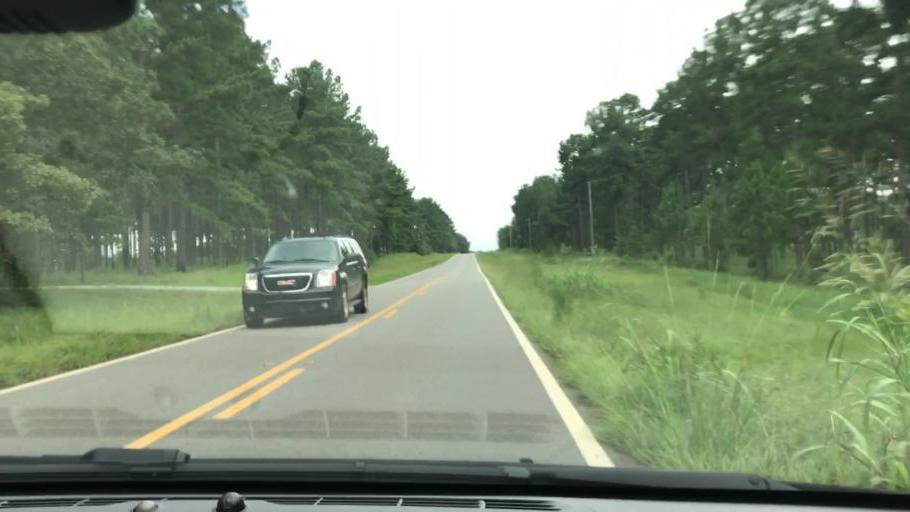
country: US
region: Georgia
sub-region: Early County
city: Blakely
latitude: 31.4568
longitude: -84.9168
